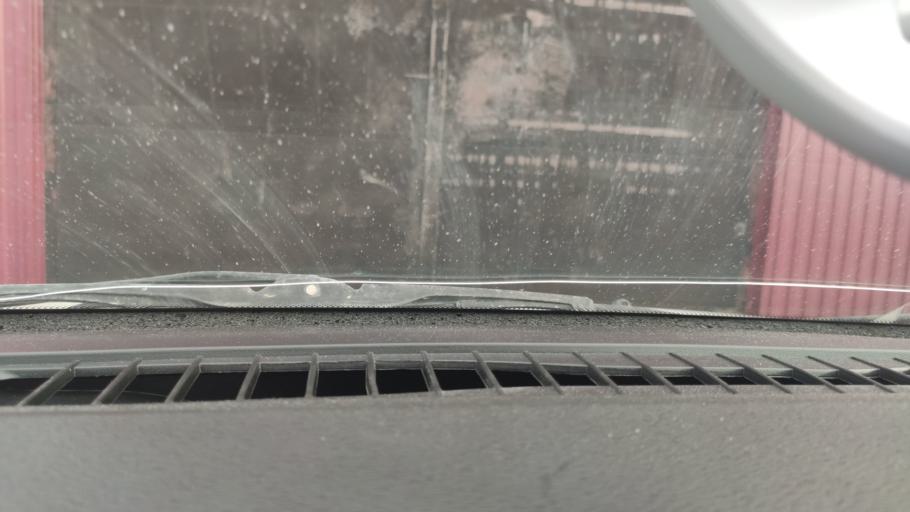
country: RU
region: Perm
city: Kultayevo
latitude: 57.9275
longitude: 56.0134
